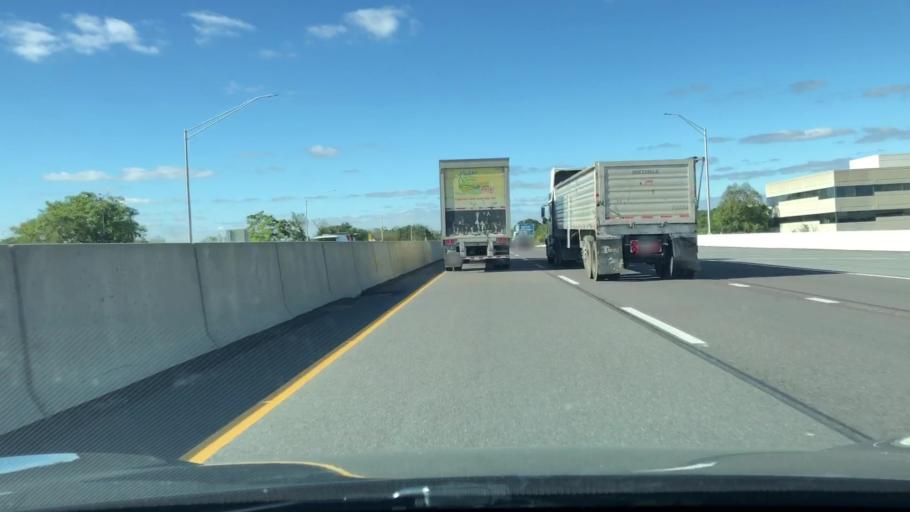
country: US
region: Pennsylvania
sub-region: Montgomery County
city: King of Prussia
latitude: 40.0913
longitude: -75.4109
